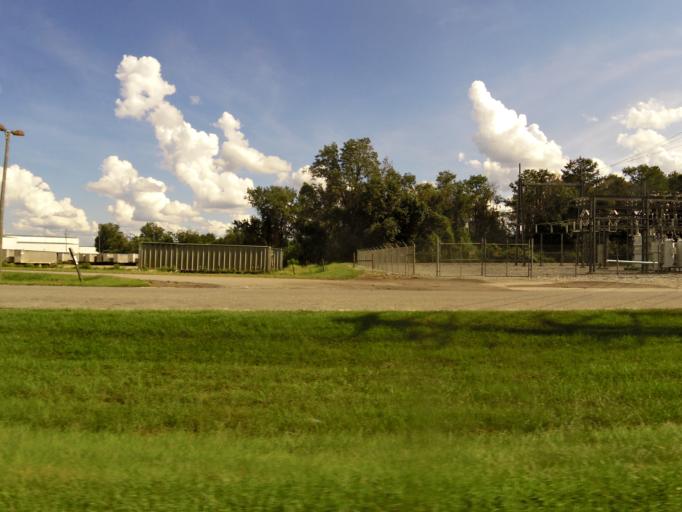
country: US
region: Georgia
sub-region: Lowndes County
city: Valdosta
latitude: 30.8142
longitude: -83.2835
